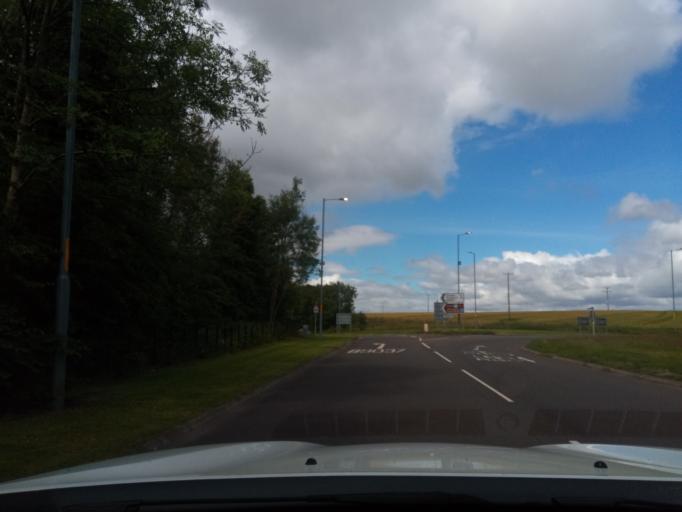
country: GB
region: Scotland
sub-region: Fife
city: Oakley
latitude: 56.0593
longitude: -3.5451
